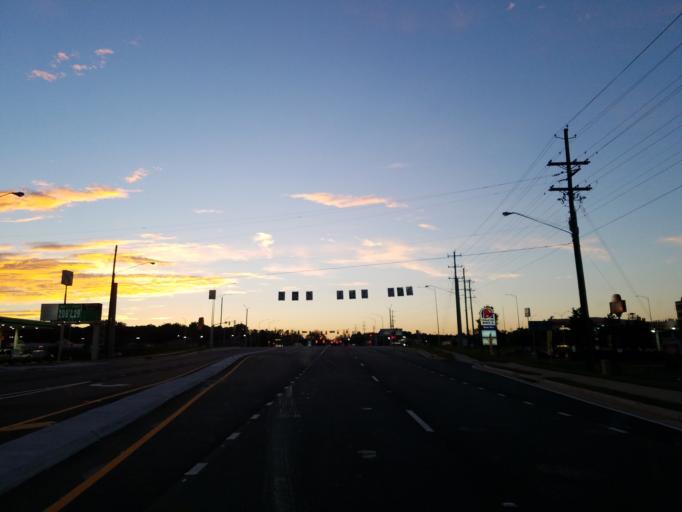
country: US
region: Georgia
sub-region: Dawson County
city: Dawsonville
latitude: 34.3621
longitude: -84.0350
